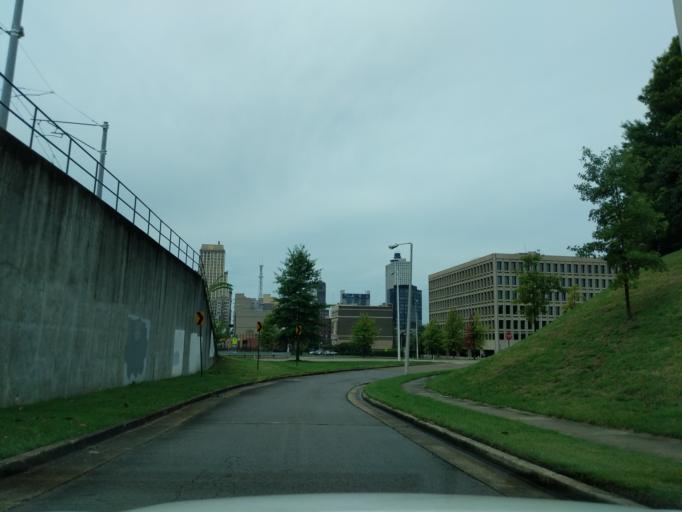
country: US
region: Tennessee
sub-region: Shelby County
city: Memphis
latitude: 35.1431
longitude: -90.0430
